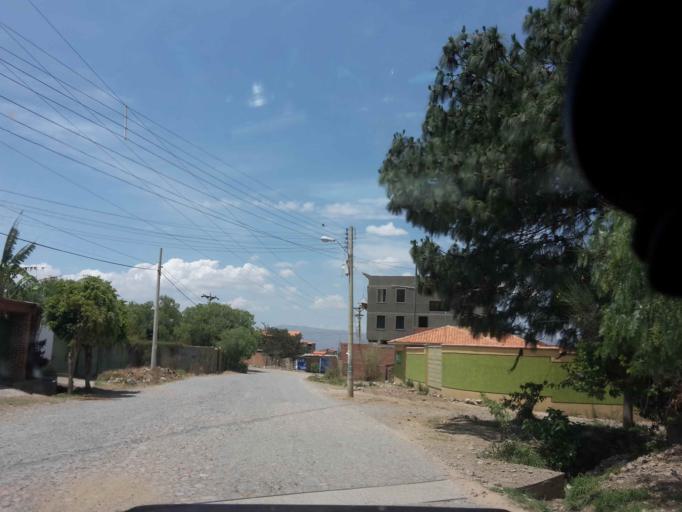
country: BO
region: Cochabamba
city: Cochabamba
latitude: -17.3312
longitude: -66.2209
